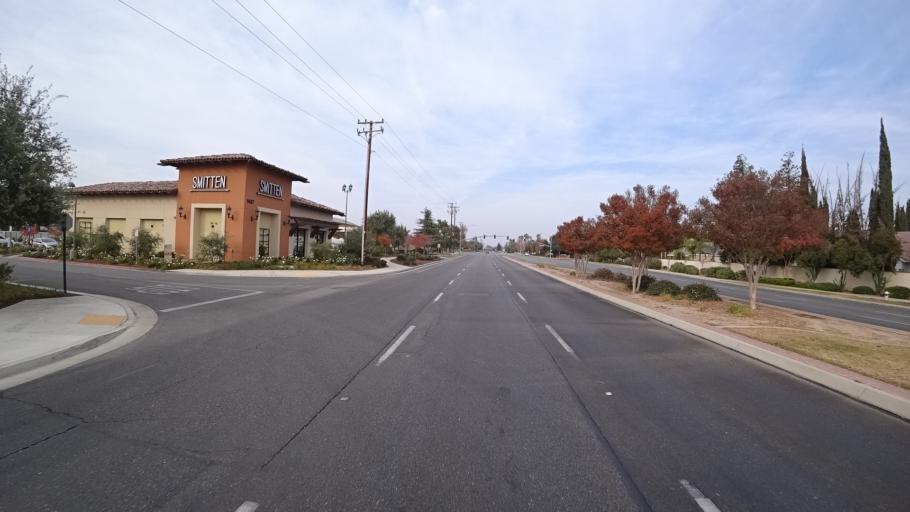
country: US
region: California
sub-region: Kern County
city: Rosedale
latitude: 35.3417
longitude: -119.1280
